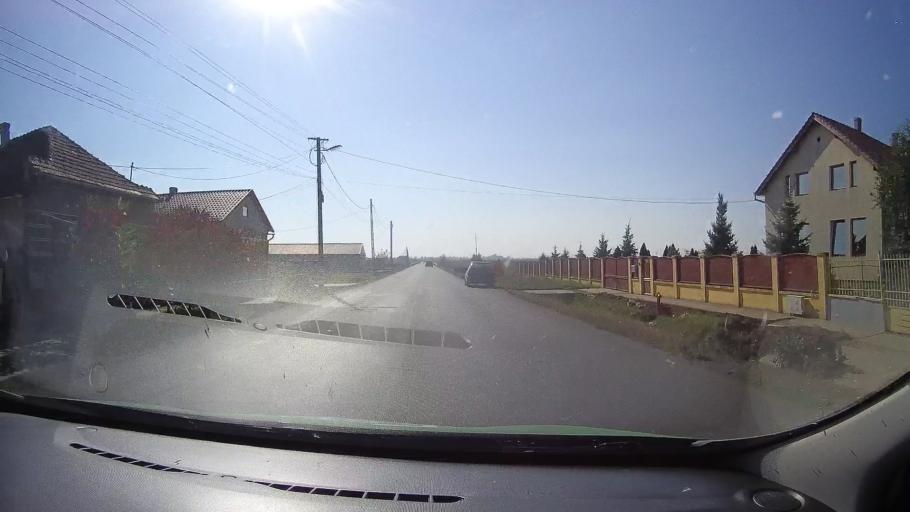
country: RO
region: Satu Mare
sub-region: Comuna Camin
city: Camin
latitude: 47.7233
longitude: 22.4758
